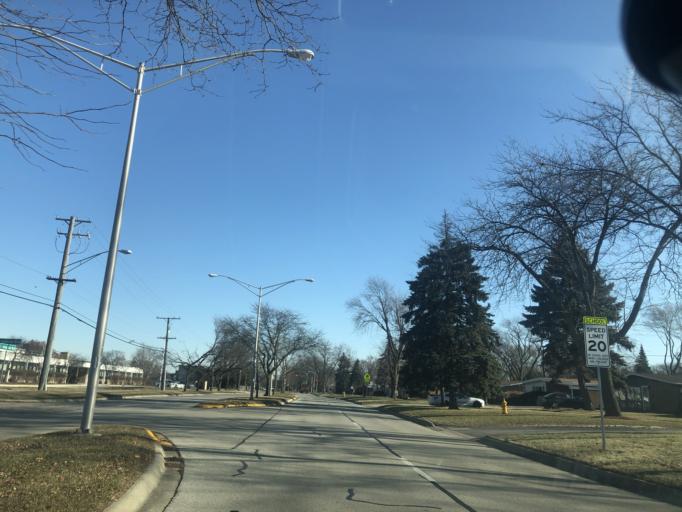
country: US
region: Illinois
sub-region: DuPage County
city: Addison
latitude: 41.9316
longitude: -87.9988
